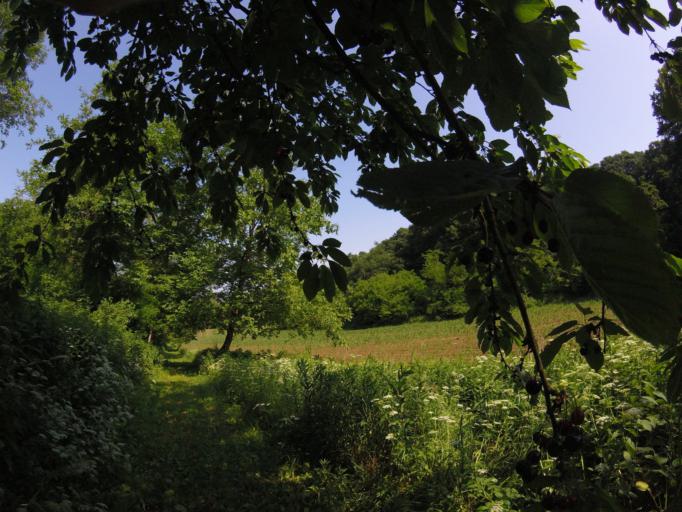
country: HU
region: Baranya
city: Harkany
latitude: 45.9044
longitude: 18.2343
